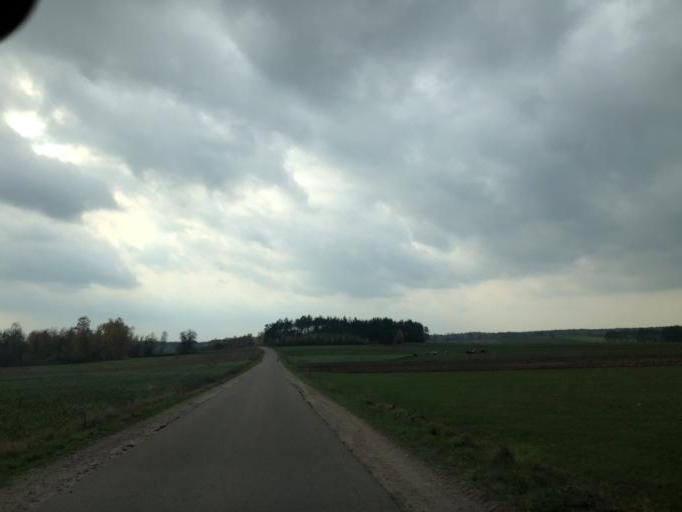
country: PL
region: Podlasie
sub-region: Lomza
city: Lomza
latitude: 53.1471
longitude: 21.9906
